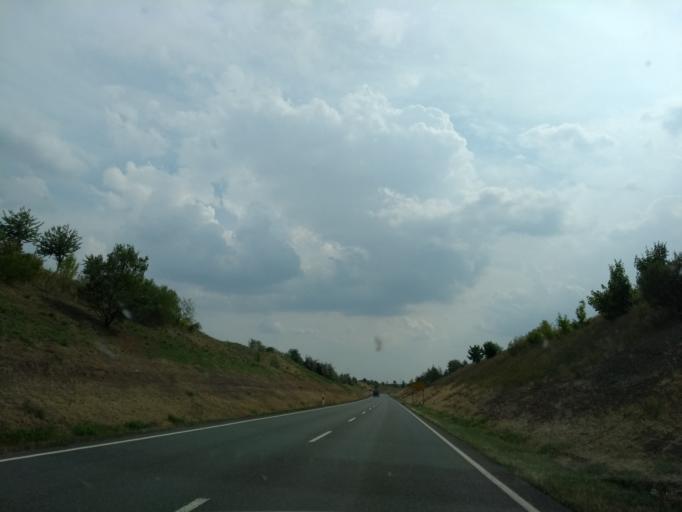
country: DE
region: Thuringia
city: Schwaara
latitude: 50.9138
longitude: 12.1335
